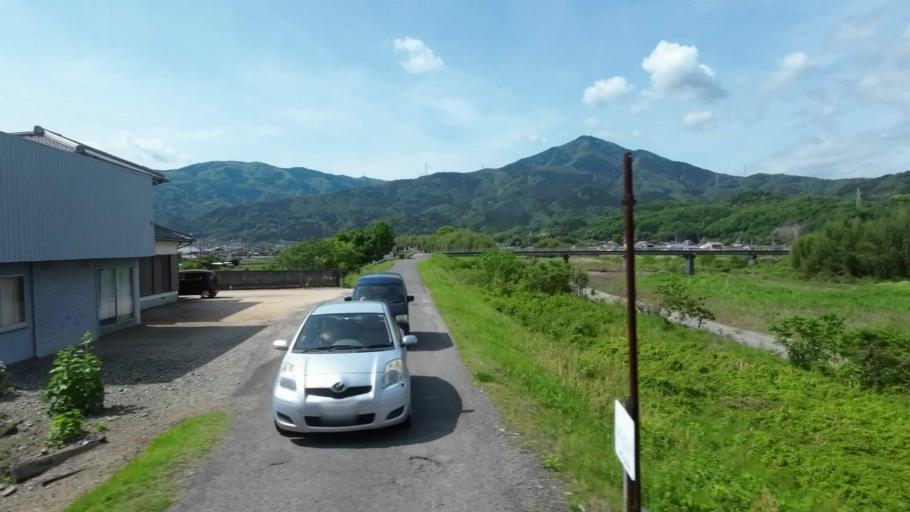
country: JP
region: Tokushima
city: Wakimachi
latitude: 34.0551
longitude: 134.2273
